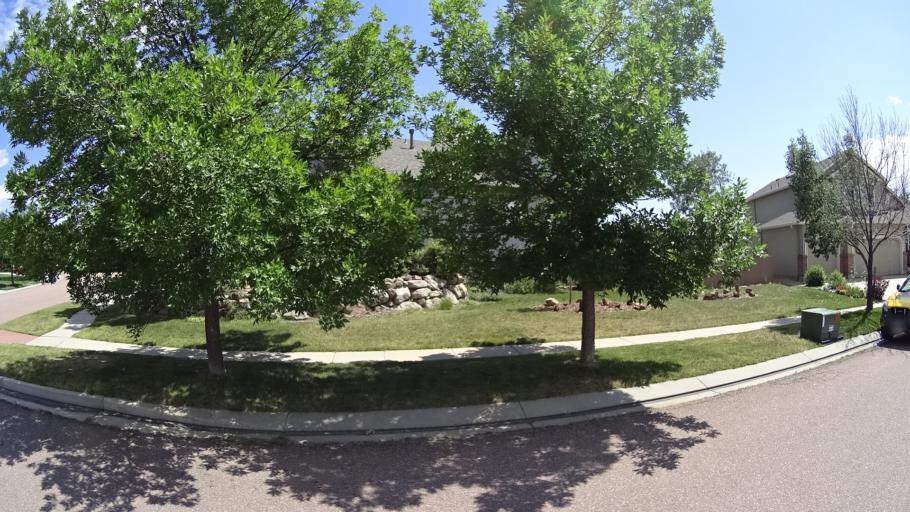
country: US
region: Colorado
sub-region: El Paso County
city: Black Forest
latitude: 38.9669
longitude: -104.7621
